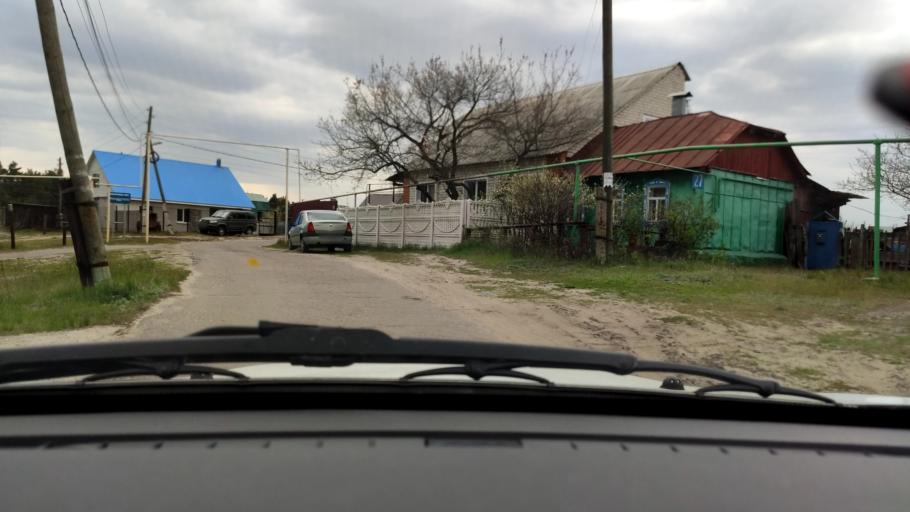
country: RU
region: Voronezj
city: Somovo
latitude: 51.7350
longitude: 39.3334
